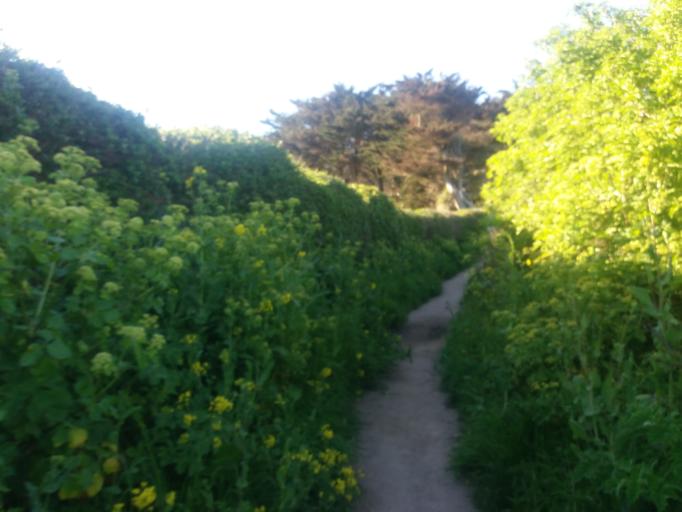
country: IE
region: Leinster
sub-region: Fingal County
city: Howth
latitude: 53.3638
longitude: -6.0723
